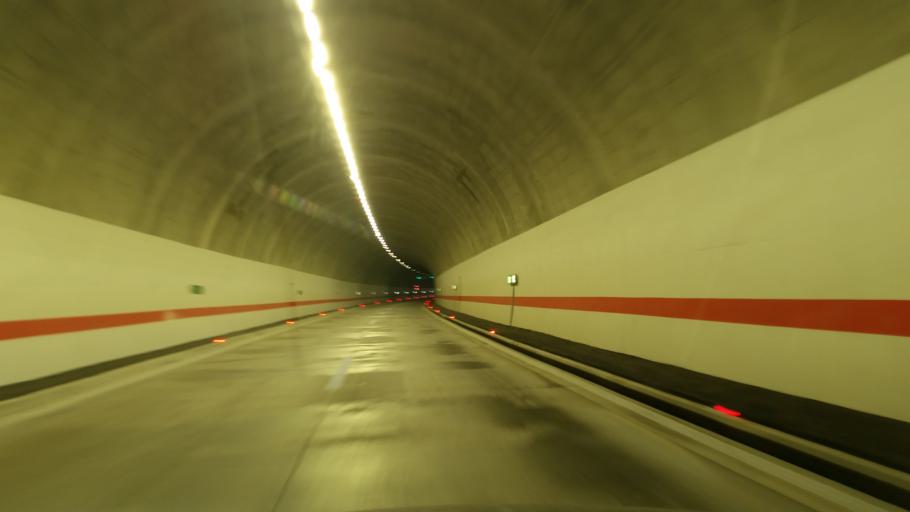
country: RS
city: Prislonica
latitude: 43.9812
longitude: 20.4022
